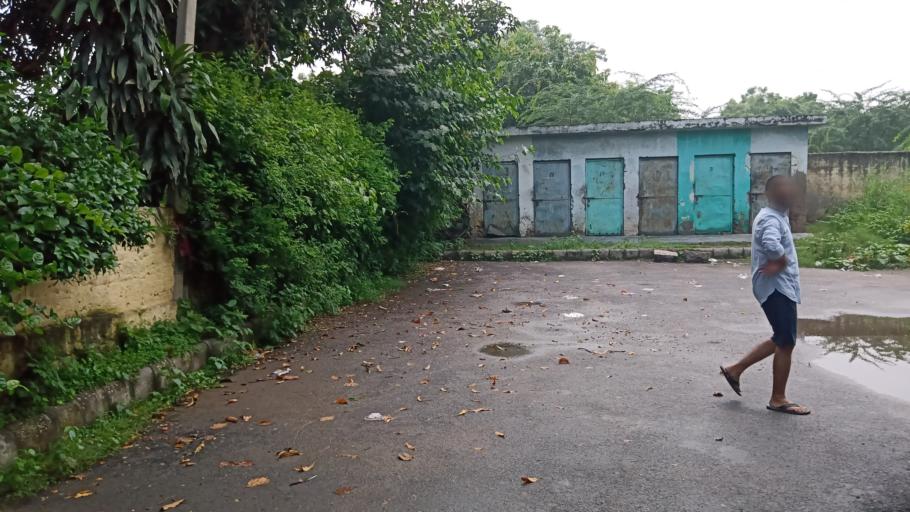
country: IN
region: NCT
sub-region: New Delhi
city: New Delhi
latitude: 28.5739
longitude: 77.2504
